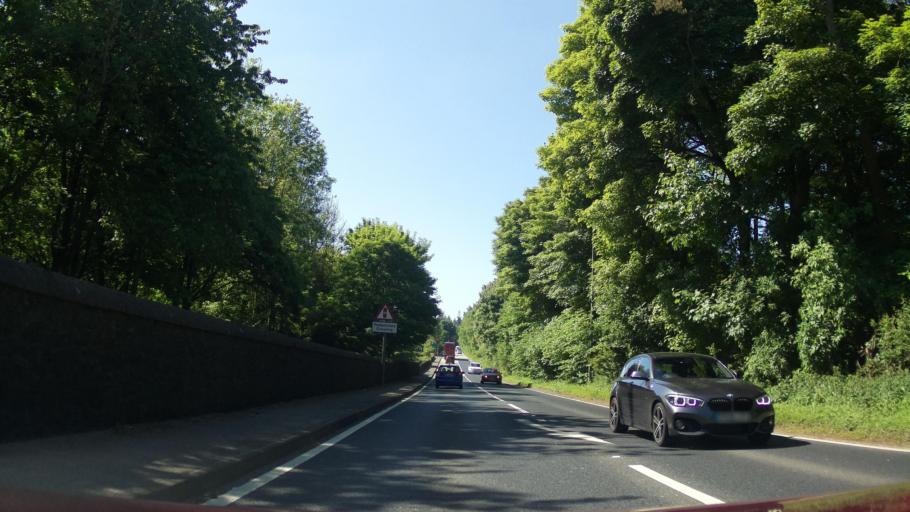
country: GB
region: Scotland
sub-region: Fife
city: Markinch
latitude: 56.2148
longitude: -3.1549
